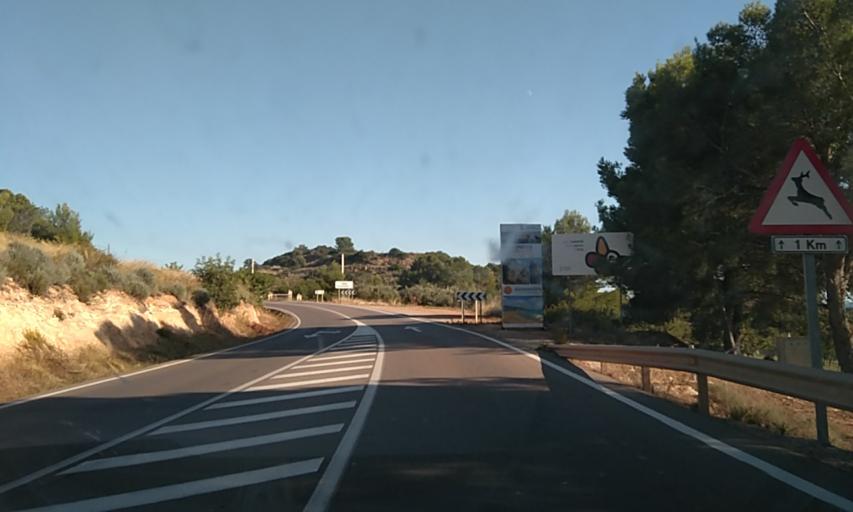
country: ES
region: Valencia
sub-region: Provincia de Castello
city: Alcoceber
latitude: 40.2496
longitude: 0.2483
